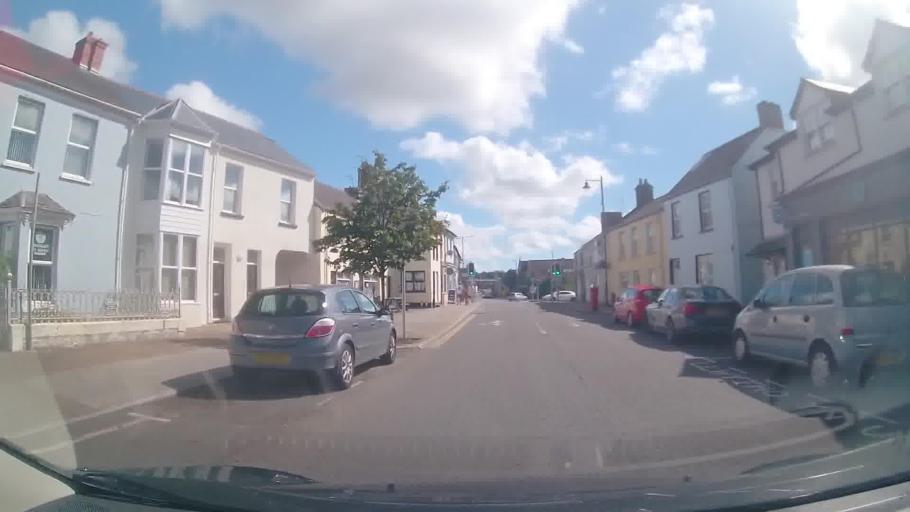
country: GB
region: Wales
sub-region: Pembrokeshire
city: Pembroke
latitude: 51.6743
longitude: -4.9098
